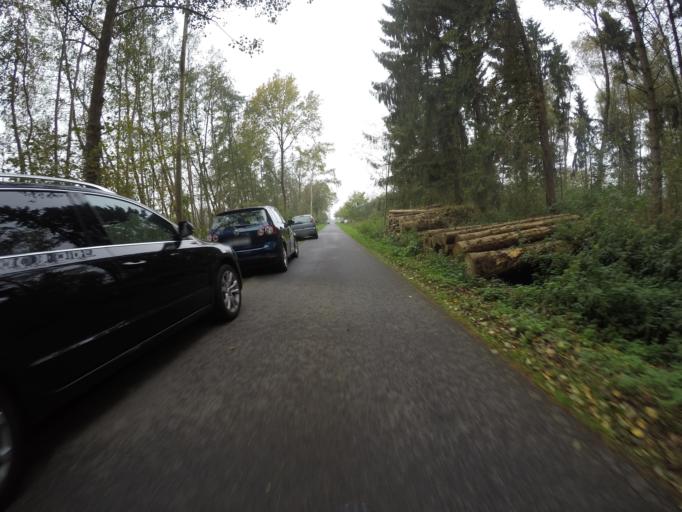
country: DE
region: North Rhine-Westphalia
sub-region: Regierungsbezirk Dusseldorf
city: Bocholt
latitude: 51.8319
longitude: 6.5544
